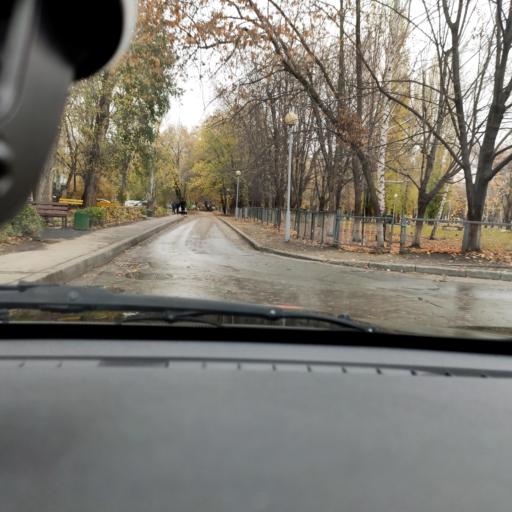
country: RU
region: Samara
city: Tol'yatti
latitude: 53.5226
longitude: 49.2827
